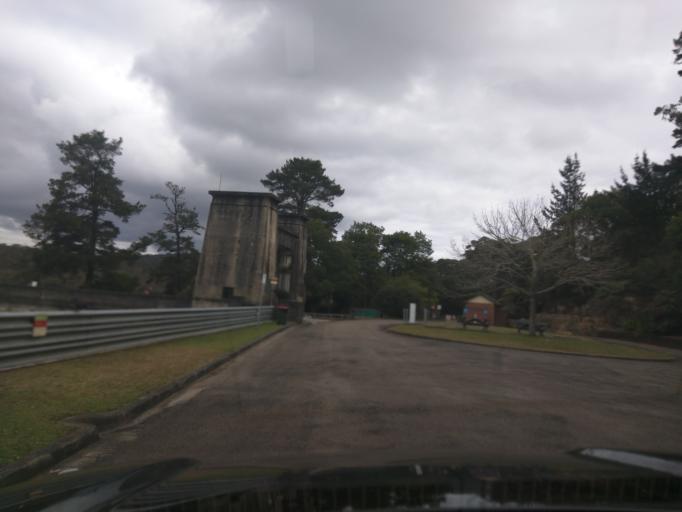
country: AU
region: New South Wales
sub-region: Wollongong
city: Mount Keira
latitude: -34.3357
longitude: 150.7458
